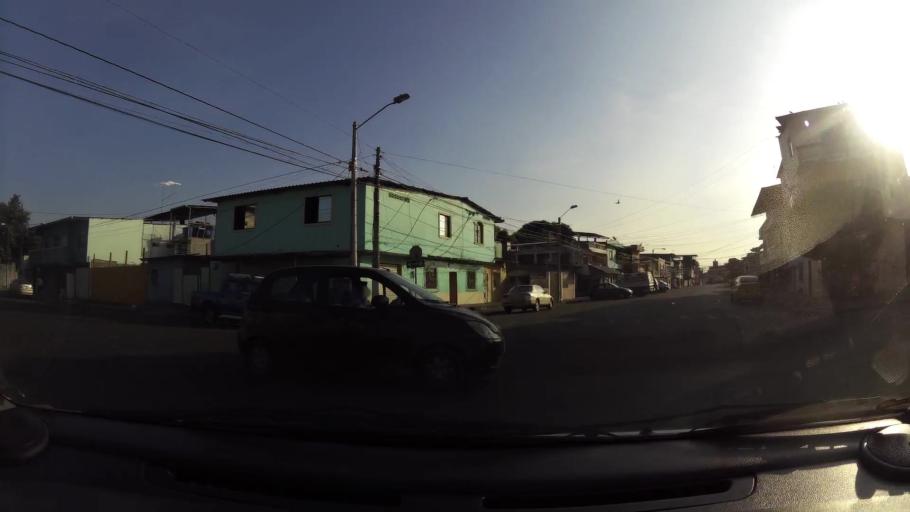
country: EC
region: Guayas
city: Eloy Alfaro
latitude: -2.1689
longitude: -79.8480
